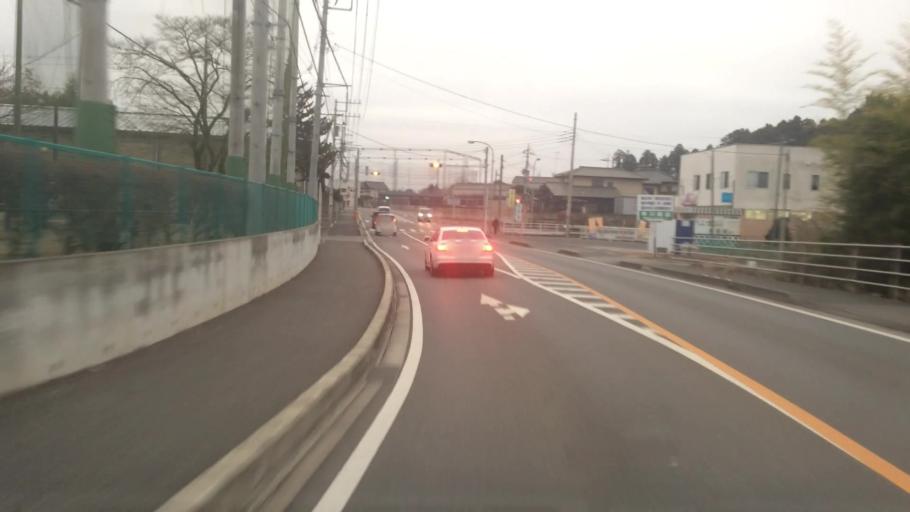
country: JP
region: Tochigi
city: Utsunomiya-shi
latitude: 36.6137
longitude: 139.8389
